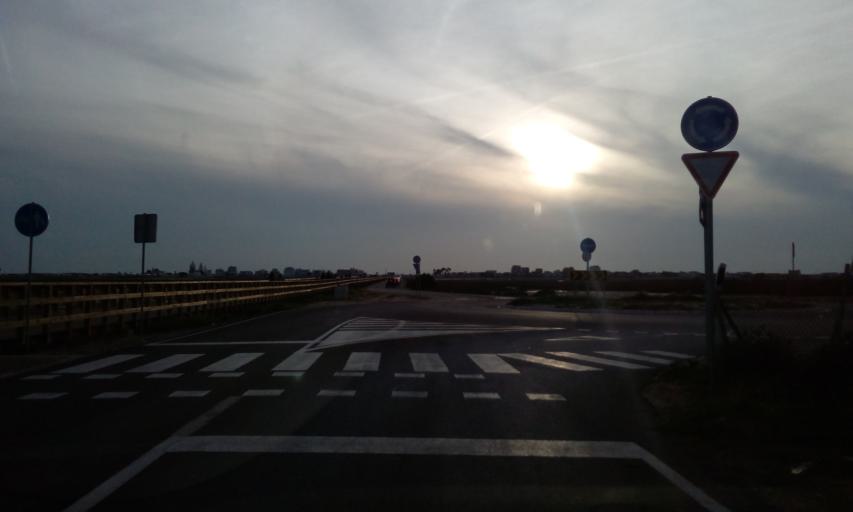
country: PT
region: Faro
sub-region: Faro
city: Faro
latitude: 37.0148
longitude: -7.9875
